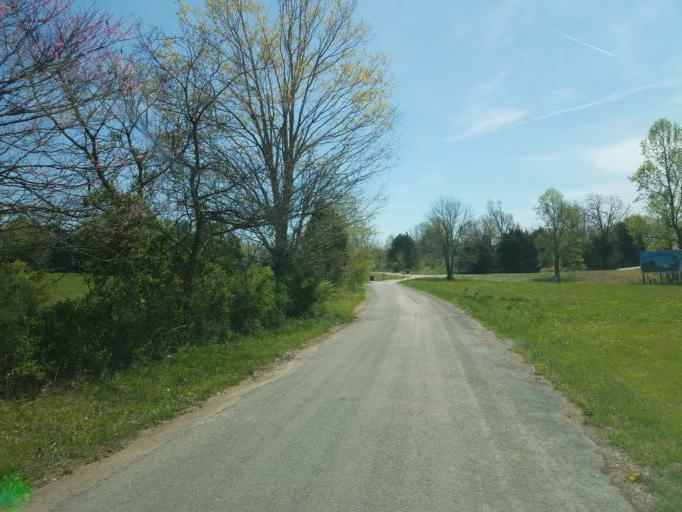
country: US
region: Kentucky
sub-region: Barren County
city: Cave City
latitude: 37.1459
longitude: -86.0388
